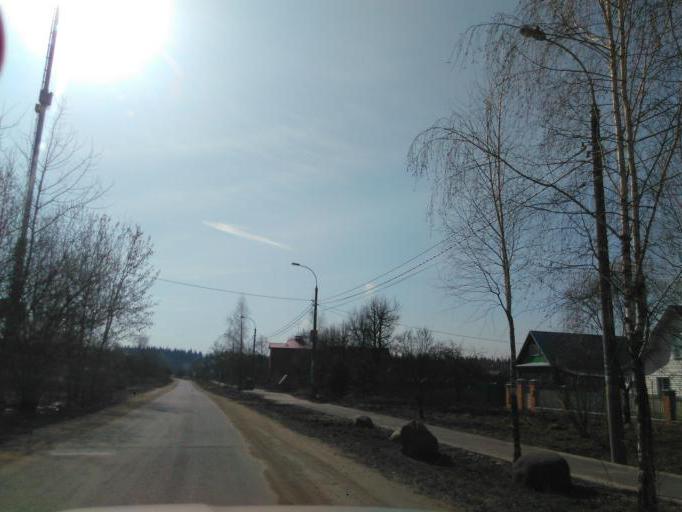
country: RU
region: Moskovskaya
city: Opalikha
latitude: 55.8777
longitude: 37.2672
